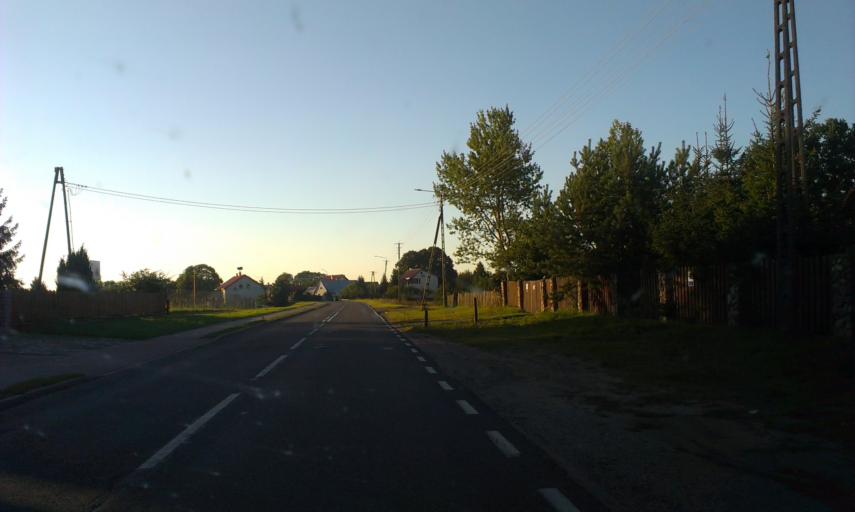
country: PL
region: Pomeranian Voivodeship
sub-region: Powiat czluchowski
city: Czarne
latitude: 53.7317
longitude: 16.8231
